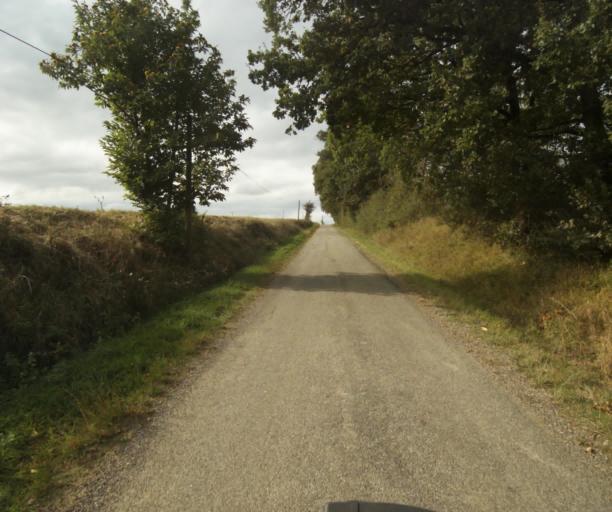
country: FR
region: Midi-Pyrenees
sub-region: Departement du Tarn-et-Garonne
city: Beaumont-de-Lomagne
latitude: 43.8242
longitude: 1.0815
